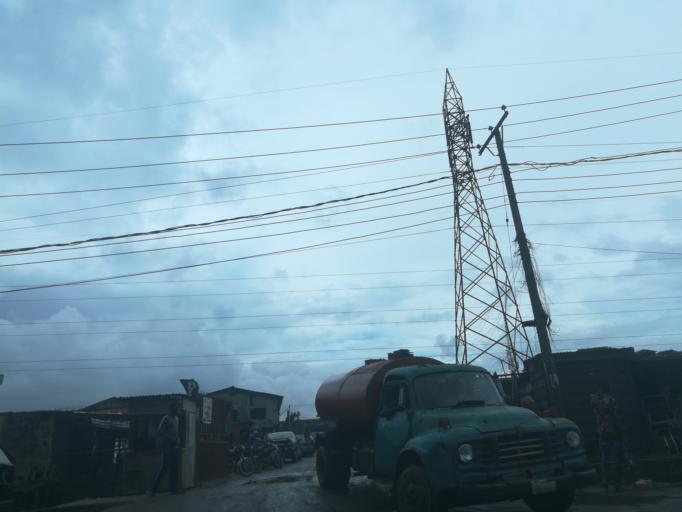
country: NG
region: Lagos
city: Agege
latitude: 6.6207
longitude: 3.3359
